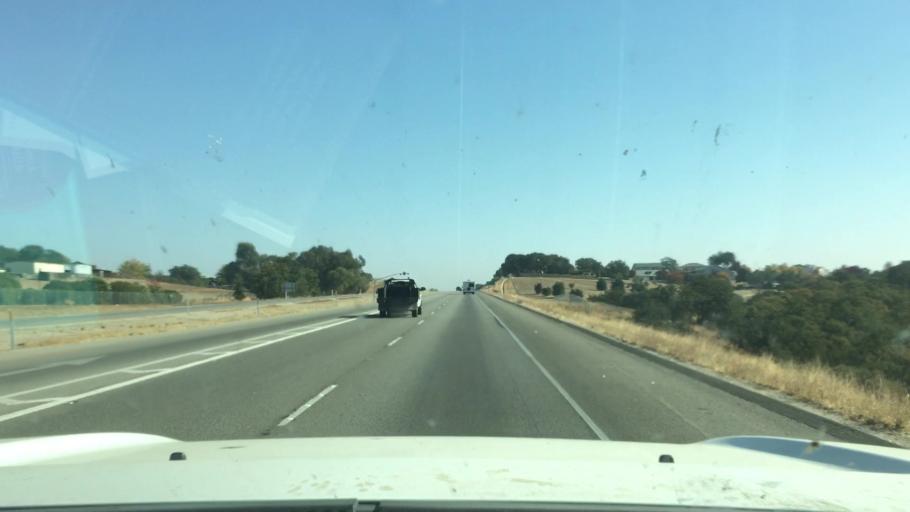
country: US
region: California
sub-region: San Luis Obispo County
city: Paso Robles
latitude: 35.6445
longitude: -120.6718
